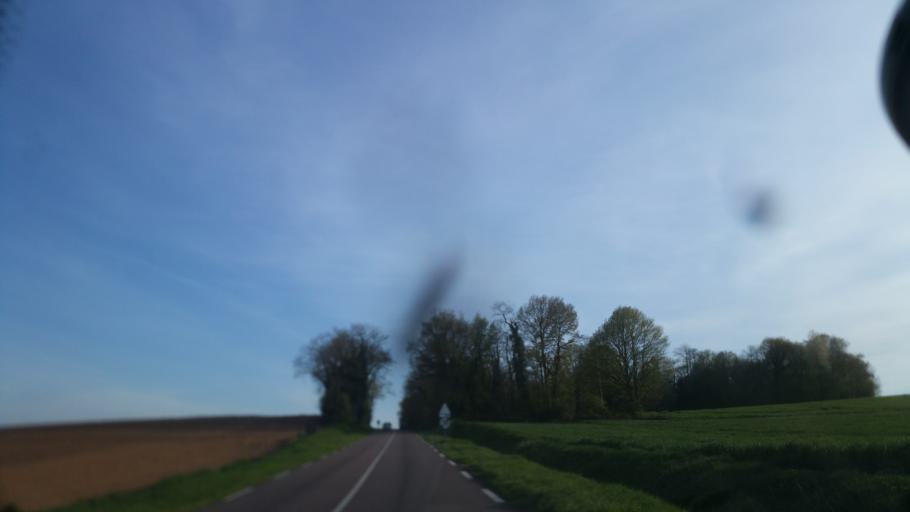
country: FR
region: Ile-de-France
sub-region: Departement de l'Essonne
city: Saint-Cyr-sous-Dourdan
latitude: 48.5661
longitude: 2.0297
